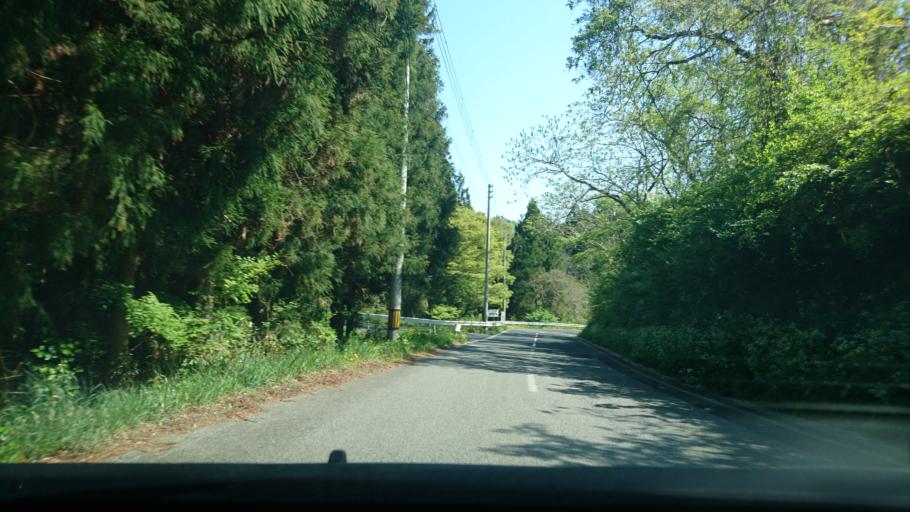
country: JP
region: Iwate
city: Ichinoseki
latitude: 38.9154
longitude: 141.2787
